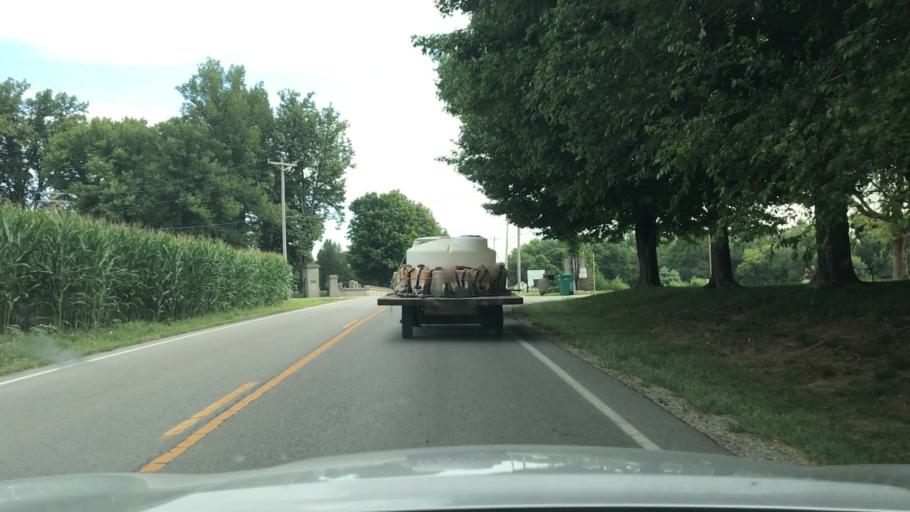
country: US
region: Kentucky
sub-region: Todd County
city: Elkton
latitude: 36.8157
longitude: -87.1524
